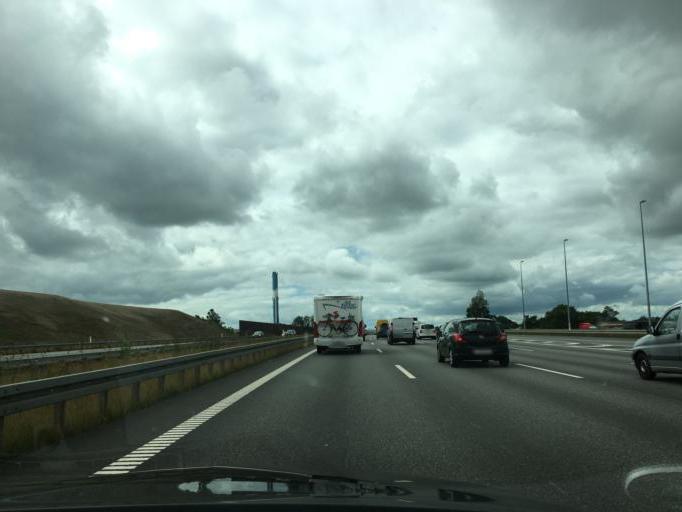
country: DK
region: Zealand
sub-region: Solrod Kommune
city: Solrod Strand
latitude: 55.5443
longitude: 12.2142
